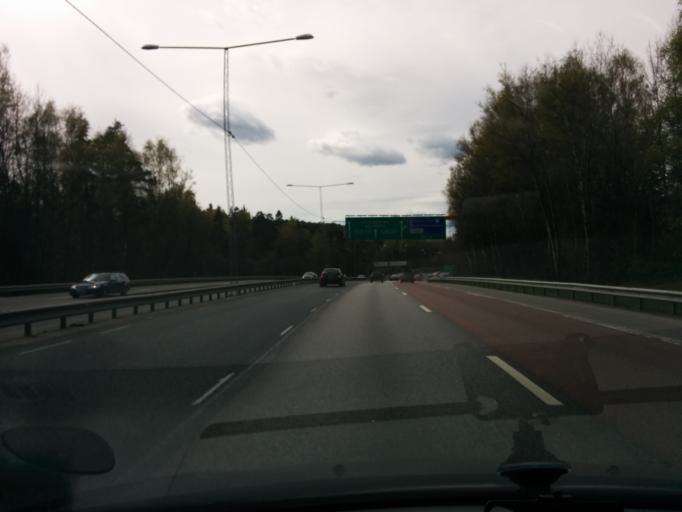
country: SE
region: Stockholm
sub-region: Botkyrka Kommun
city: Fittja
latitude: 59.2587
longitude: 17.8882
